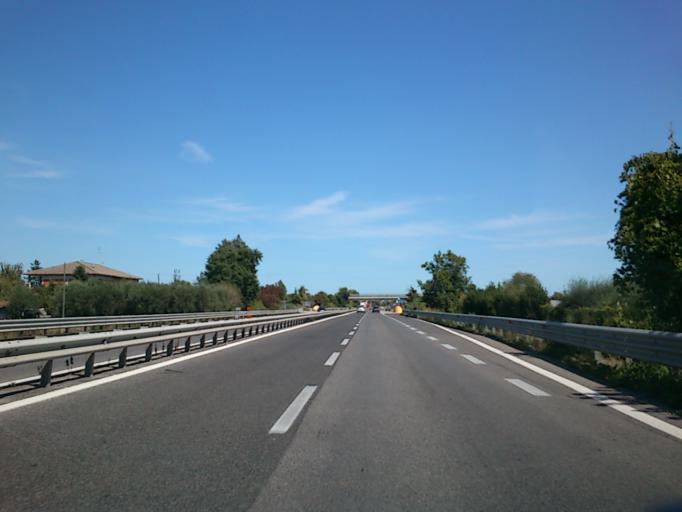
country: IT
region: The Marches
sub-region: Provincia di Pesaro e Urbino
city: Bellocchi
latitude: 43.7865
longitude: 12.9937
